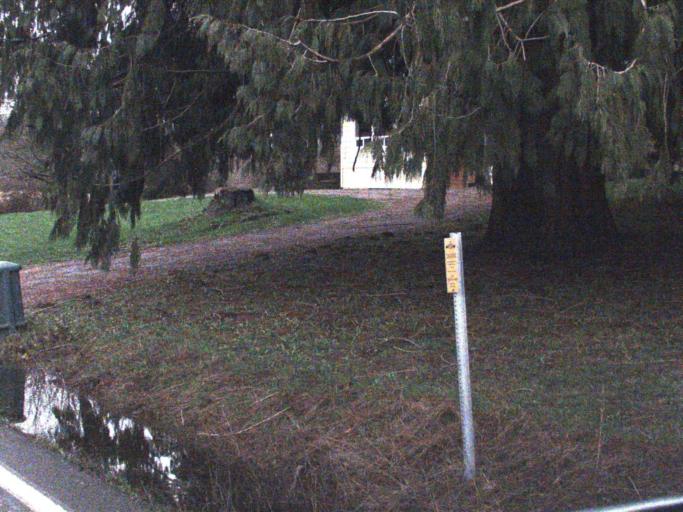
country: US
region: Washington
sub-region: Snohomish County
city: Smokey Point
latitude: 48.1520
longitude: -122.2241
